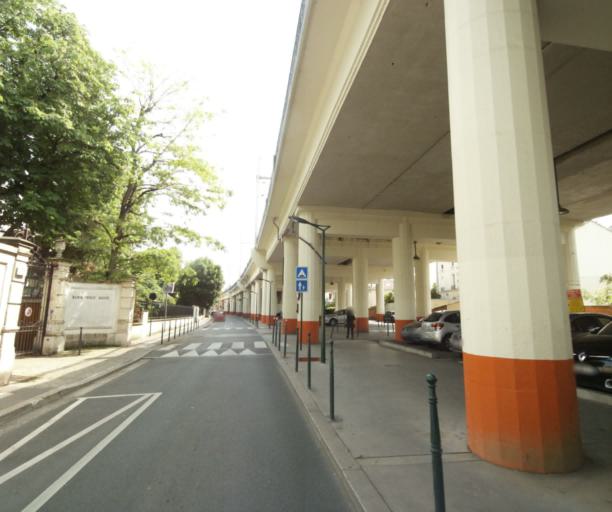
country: FR
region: Ile-de-France
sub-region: Departement des Hauts-de-Seine
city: Colombes
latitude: 48.9259
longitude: 2.2591
